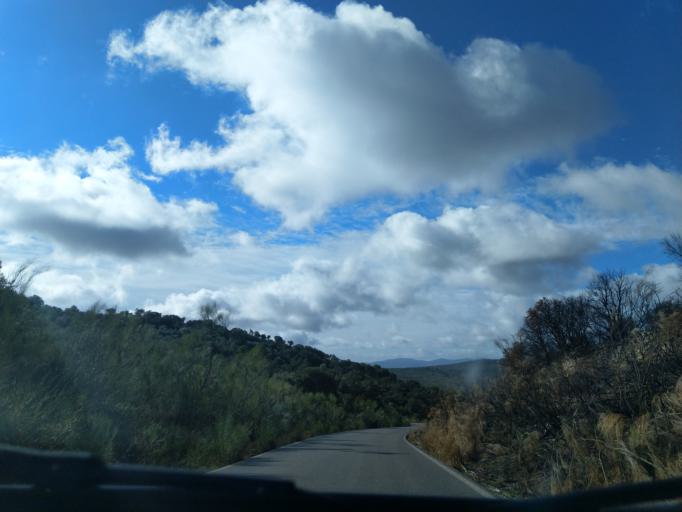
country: ES
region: Extremadura
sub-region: Provincia de Badajoz
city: Reina
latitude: 38.1466
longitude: -5.9131
